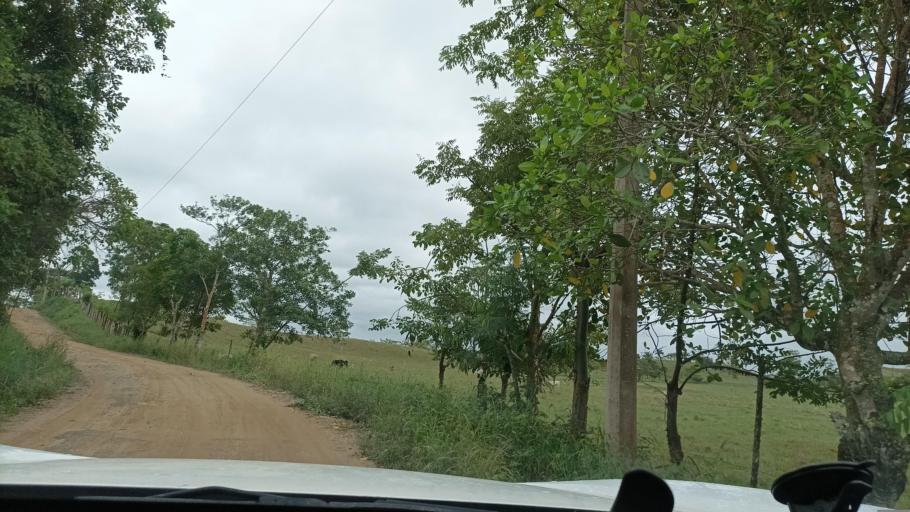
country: MX
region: Veracruz
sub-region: Moloacan
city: Cuichapa
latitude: 17.7964
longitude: -94.3785
